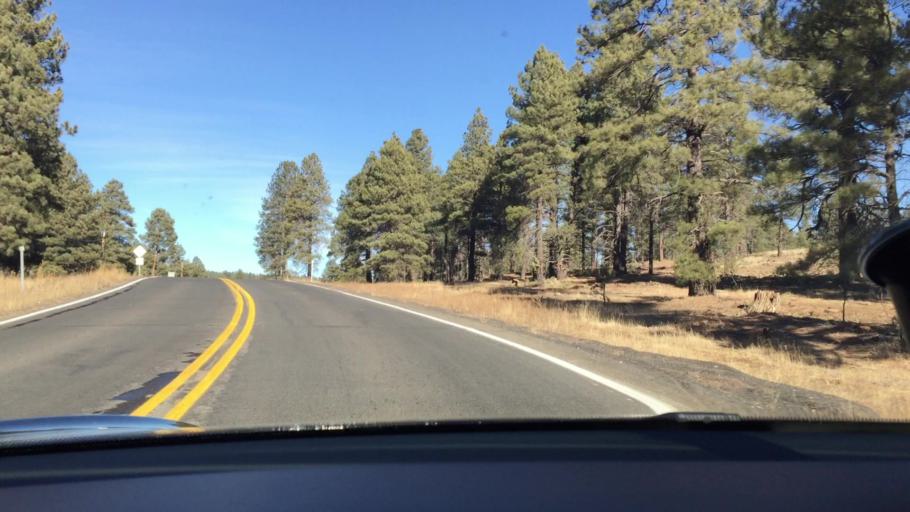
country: US
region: Arizona
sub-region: Coconino County
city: Kachina Village
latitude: 35.0896
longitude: -111.6828
